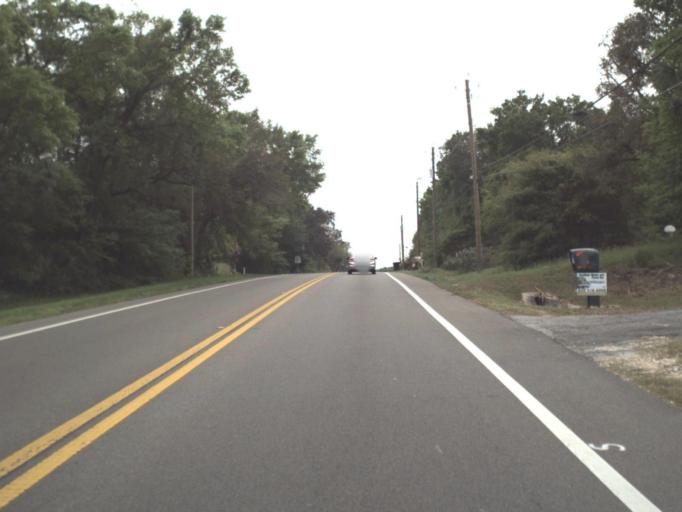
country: US
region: Florida
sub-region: Escambia County
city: East Pensacola Heights
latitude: 30.4615
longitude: -87.1643
